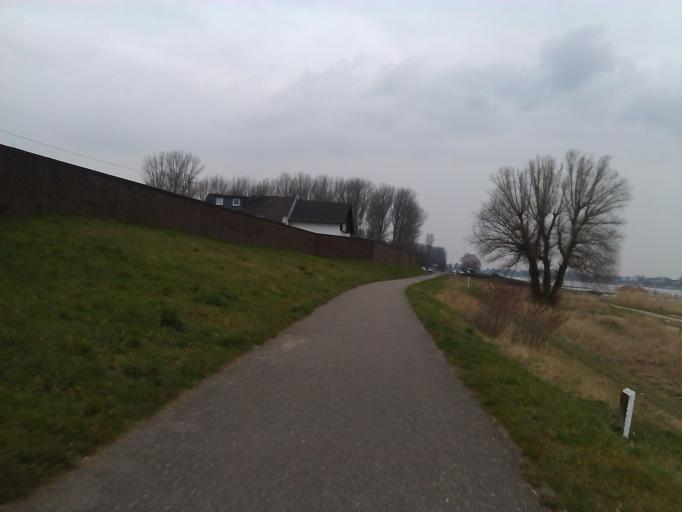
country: DE
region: North Rhine-Westphalia
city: Monheim am Rhein
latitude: 51.0519
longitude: 6.9173
